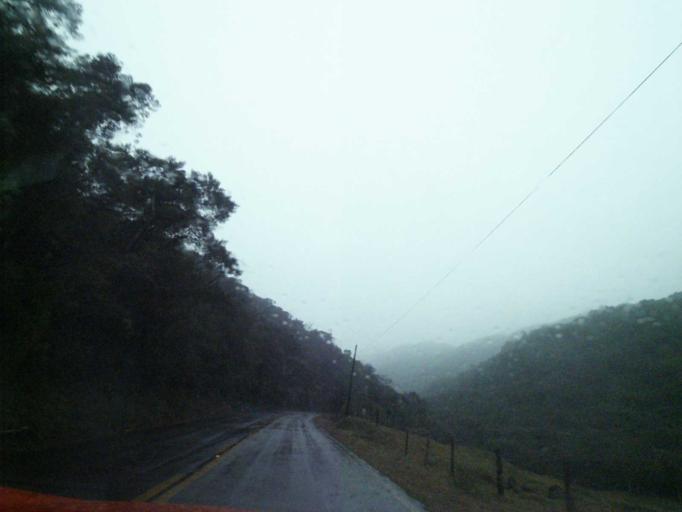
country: BR
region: Santa Catarina
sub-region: Anitapolis
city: Anitapolis
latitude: -27.7588
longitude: -49.0367
